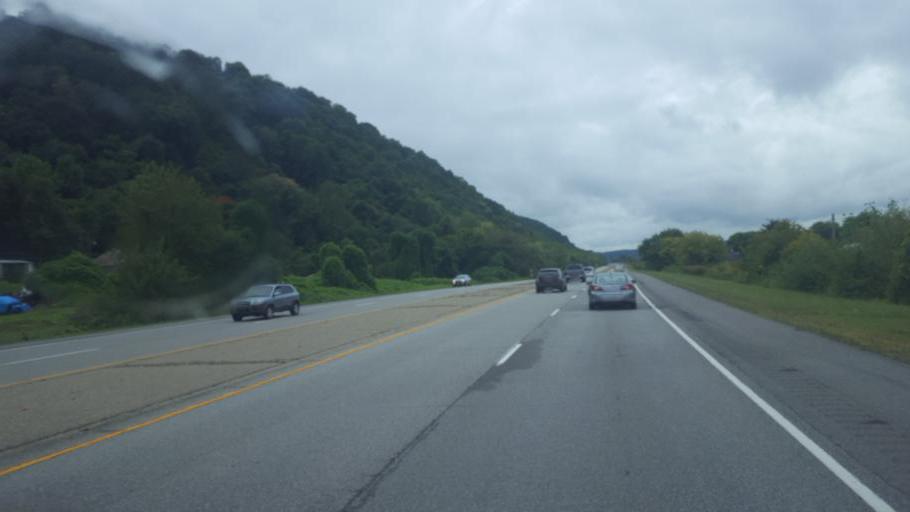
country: US
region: Kentucky
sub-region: Greenup County
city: South Shore
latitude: 38.7207
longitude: -82.9740
